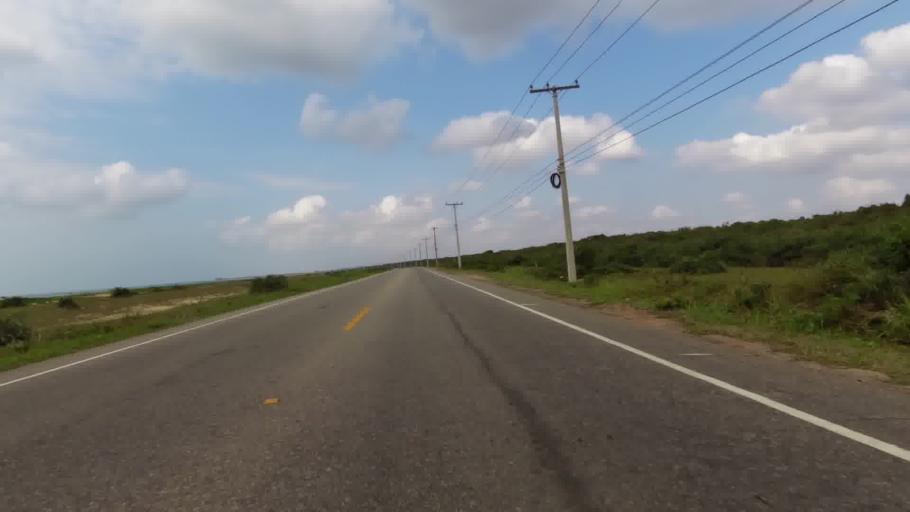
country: BR
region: Espirito Santo
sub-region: Itapemirim
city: Itapemirim
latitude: -20.9539
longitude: -40.8082
